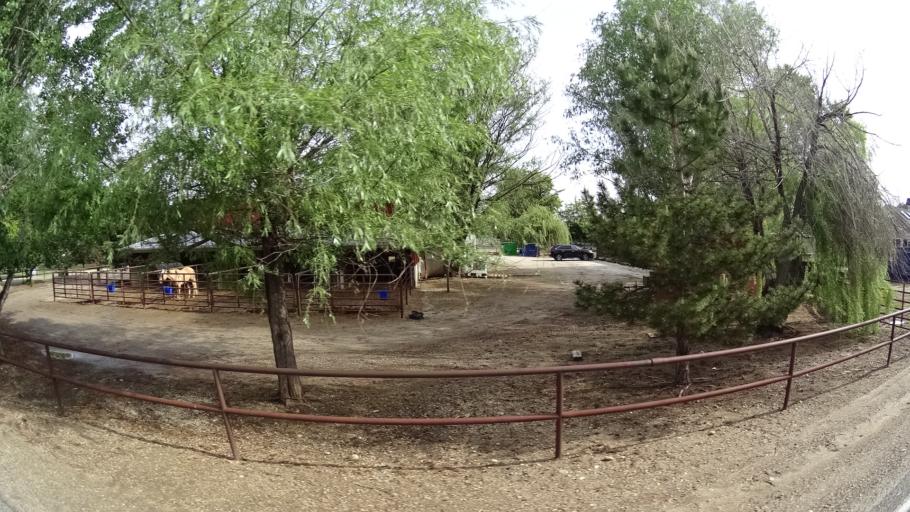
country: US
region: Idaho
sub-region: Ada County
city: Eagle
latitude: 43.7209
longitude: -116.4085
